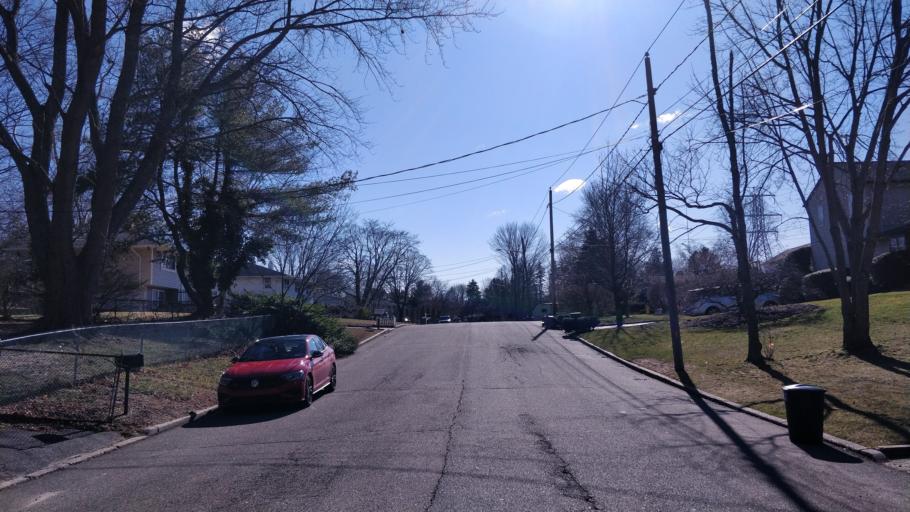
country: US
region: New York
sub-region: Suffolk County
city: Setauket-East Setauket
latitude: 40.9250
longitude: -73.0865
